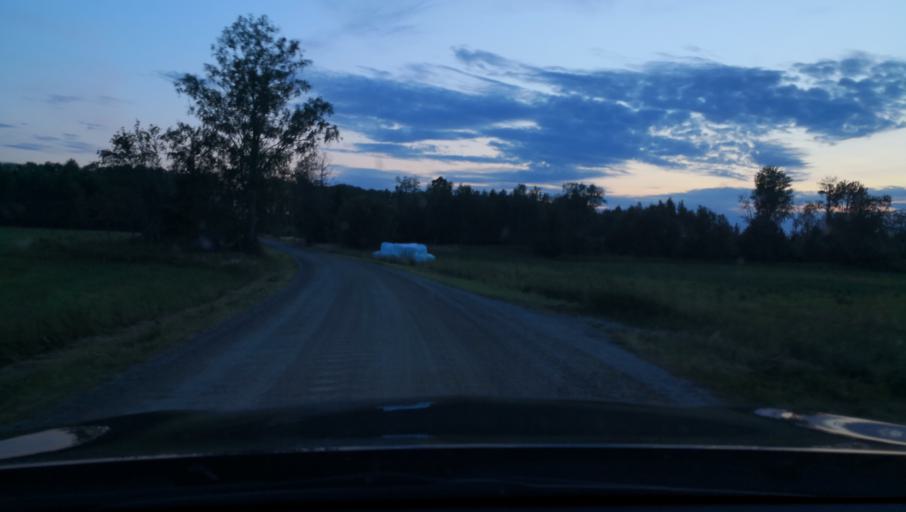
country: SE
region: Uppsala
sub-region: Osthammars Kommun
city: Bjorklinge
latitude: 60.0032
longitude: 17.3508
